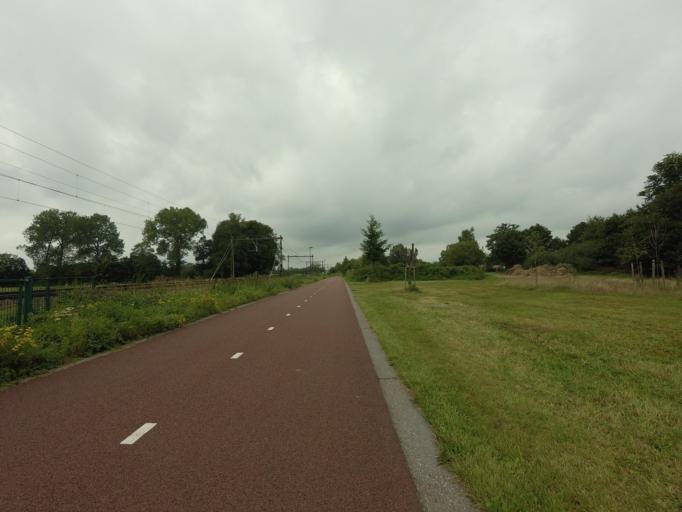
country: NL
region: Overijssel
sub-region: Gemeente Borne
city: Borne
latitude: 52.2806
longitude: 6.7668
